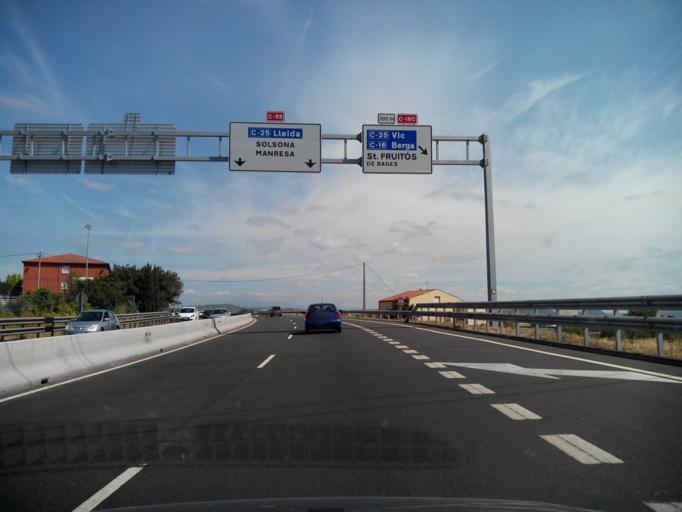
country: ES
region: Catalonia
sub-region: Provincia de Barcelona
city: Sant Fruitos de Bages
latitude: 41.7315
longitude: 1.8520
